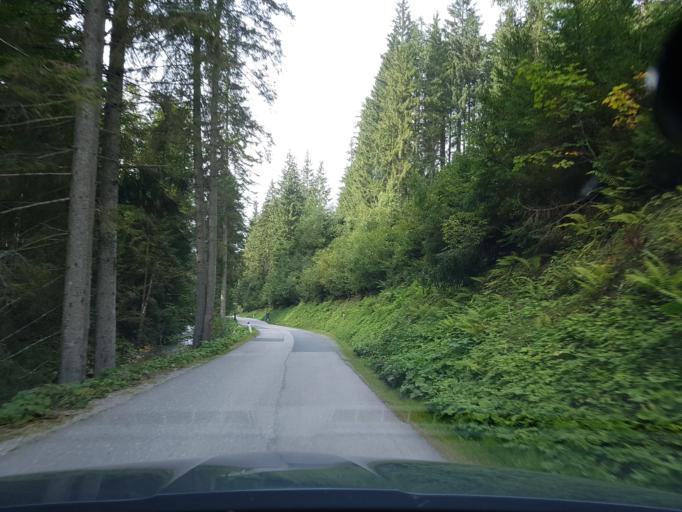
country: AT
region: Salzburg
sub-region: Politischer Bezirk Sankt Johann im Pongau
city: Forstau
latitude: 47.3546
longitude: 13.5698
